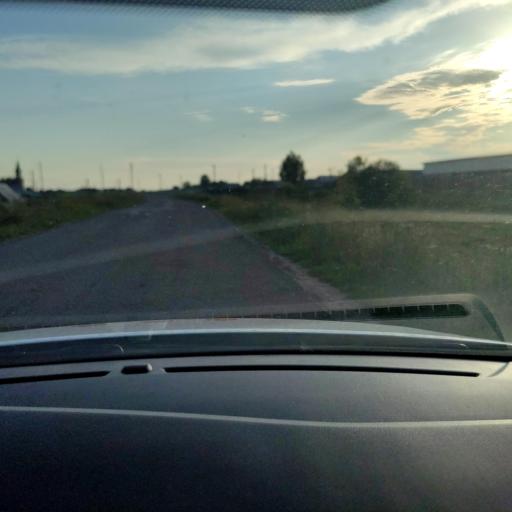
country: RU
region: Tatarstan
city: Vysokaya Gora
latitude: 55.9699
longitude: 49.2892
